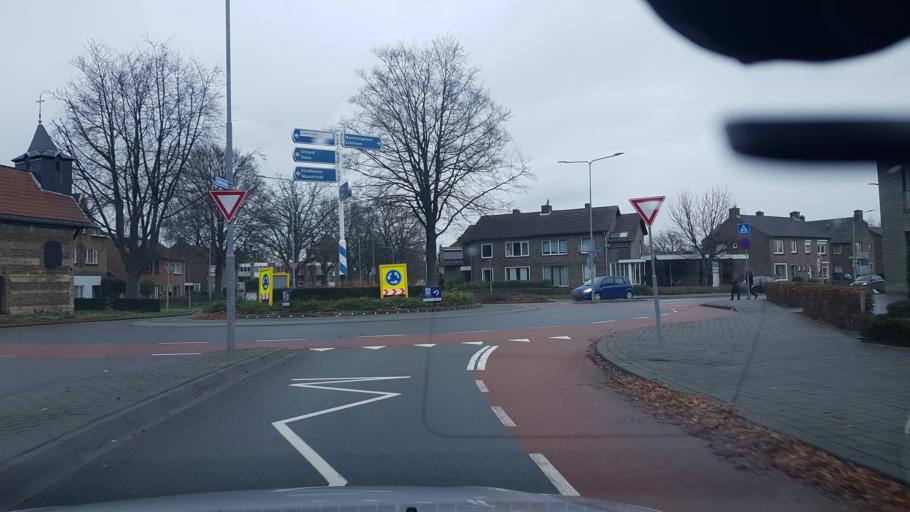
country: NL
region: Limburg
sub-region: Gemeente Beek
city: Beek
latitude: 50.9598
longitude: 5.8331
